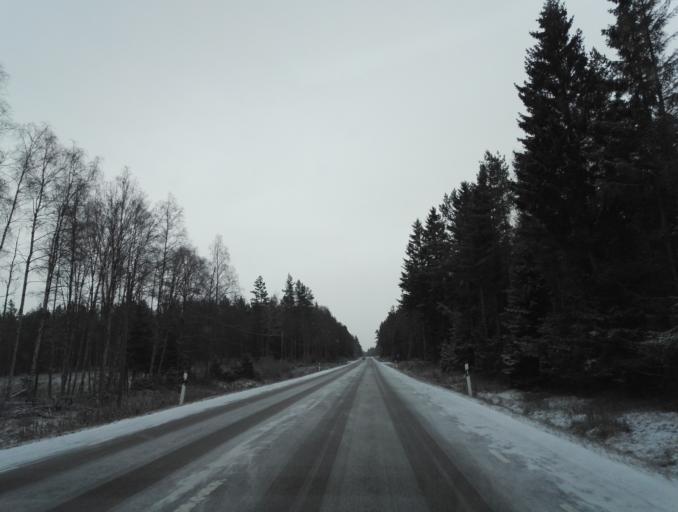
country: SE
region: Kronoberg
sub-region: Uppvidinge Kommun
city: Lenhovda
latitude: 56.9695
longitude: 15.3081
